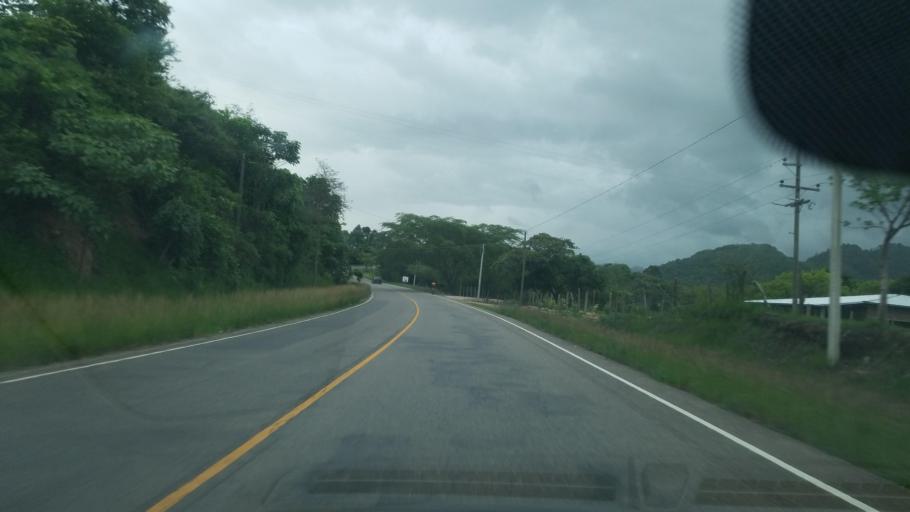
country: HN
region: Ocotepeque
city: Sinuapa
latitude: 14.5038
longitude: -89.2263
